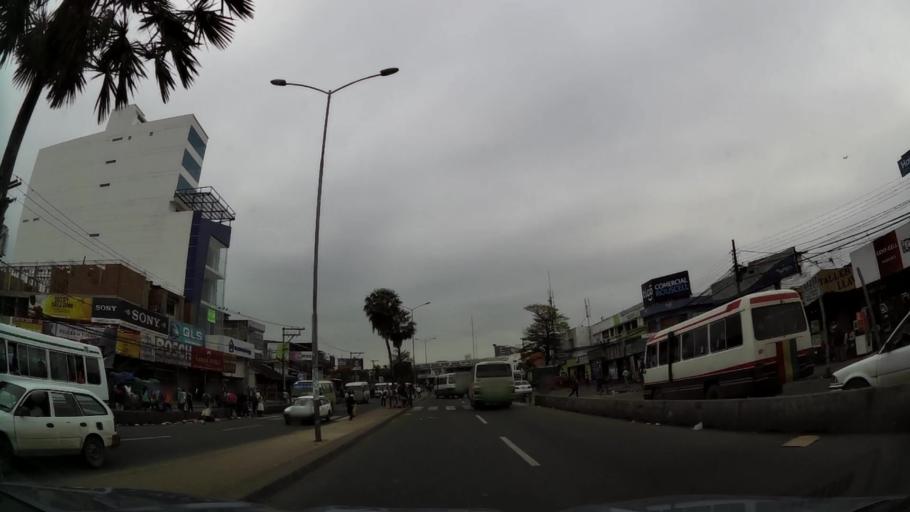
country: BO
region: Santa Cruz
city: Santa Cruz de la Sierra
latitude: -17.7940
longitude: -63.1881
